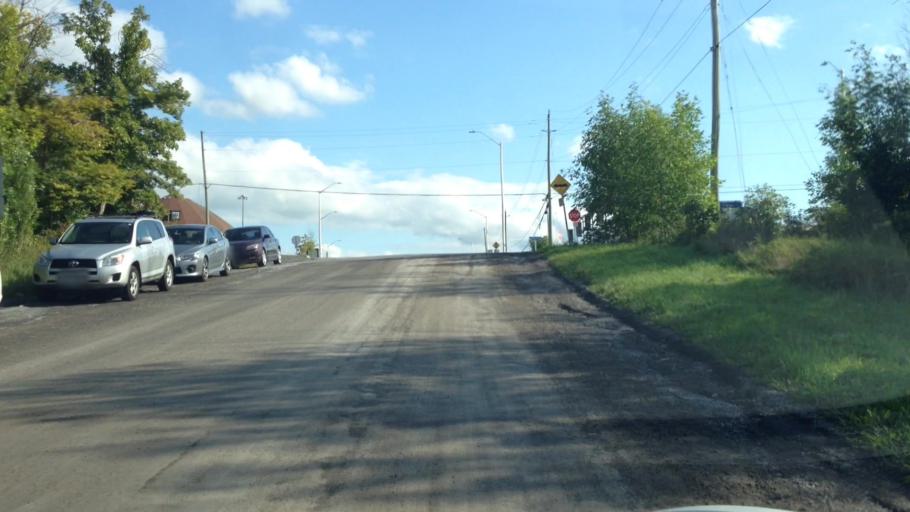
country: CA
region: Ontario
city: Clarence-Rockland
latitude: 45.4977
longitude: -75.4836
